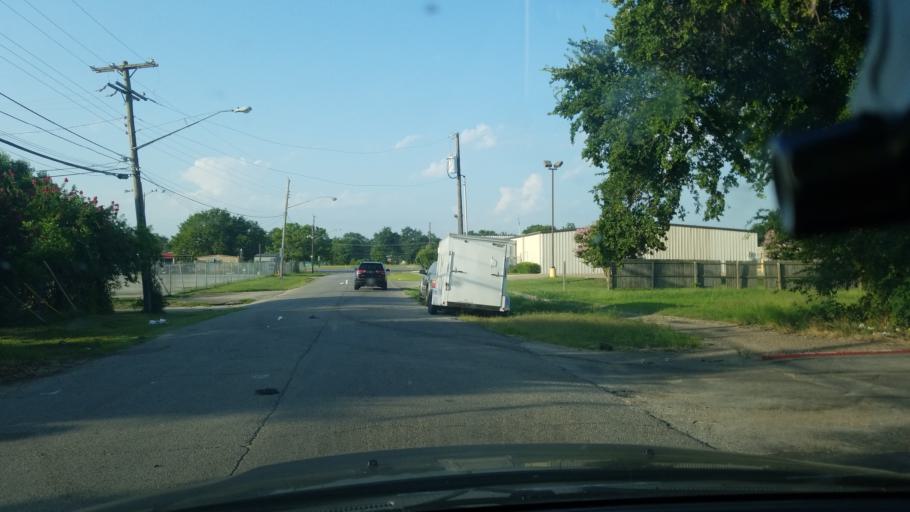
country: US
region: Texas
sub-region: Dallas County
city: Balch Springs
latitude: 32.7137
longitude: -96.6885
